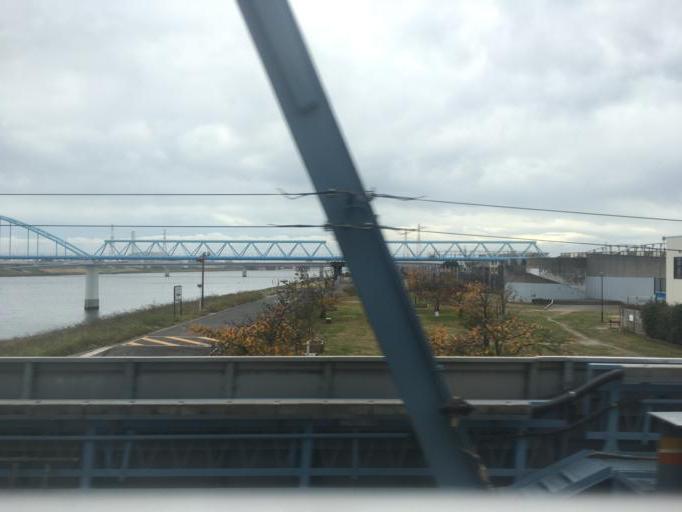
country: JP
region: Tokyo
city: Urayasu
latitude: 35.6958
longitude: 139.9308
